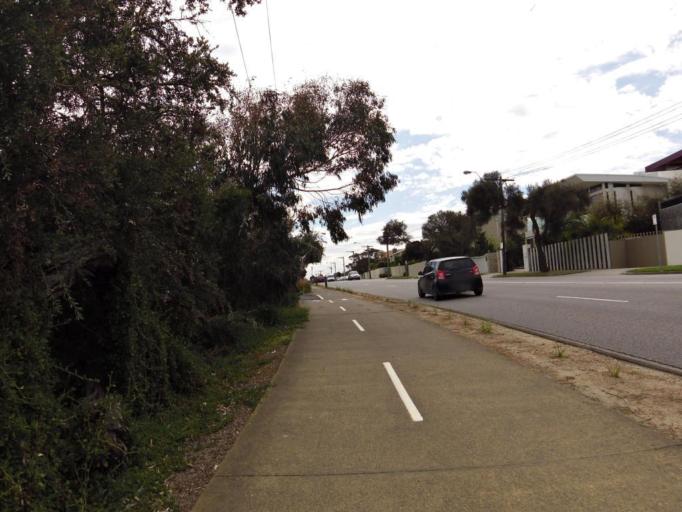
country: AU
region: Victoria
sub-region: Bayside
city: Black Rock
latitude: -37.9676
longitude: 145.0121
